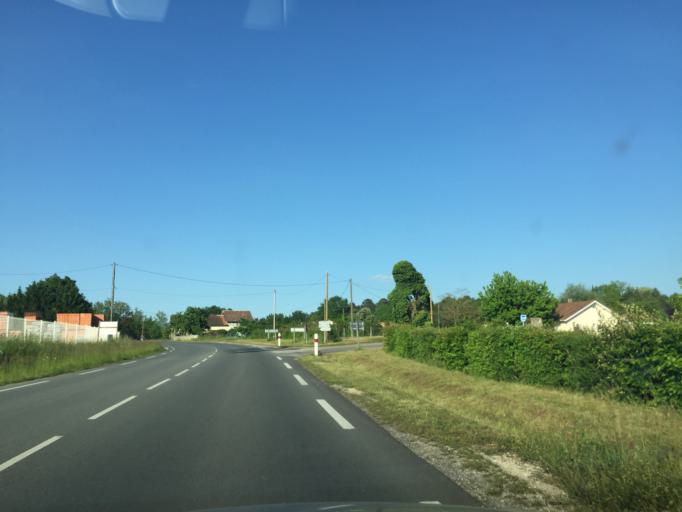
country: FR
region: Aquitaine
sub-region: Departement de la Dordogne
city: La Roche-Chalais
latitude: 45.1637
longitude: 0.0089
